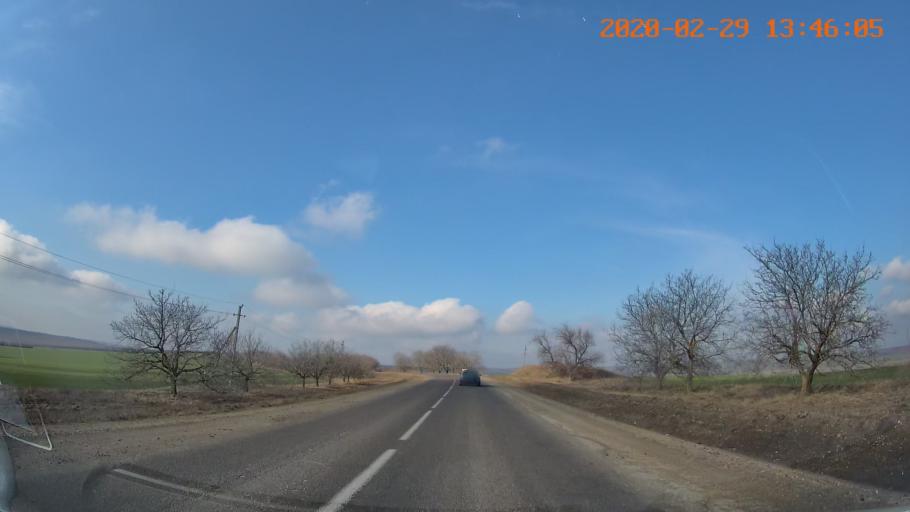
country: MD
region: Floresti
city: Leninskiy
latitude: 47.8540
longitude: 28.5102
